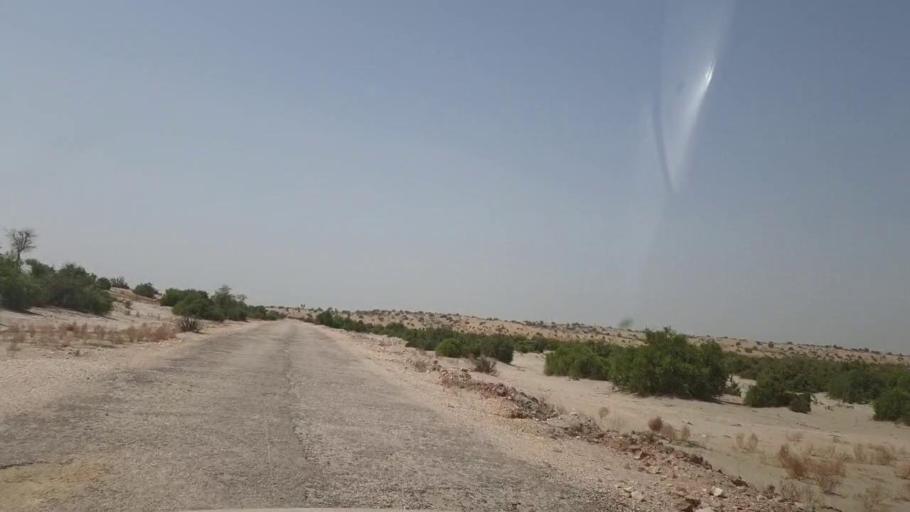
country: PK
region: Sindh
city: Khanpur
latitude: 27.3563
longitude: 69.3180
